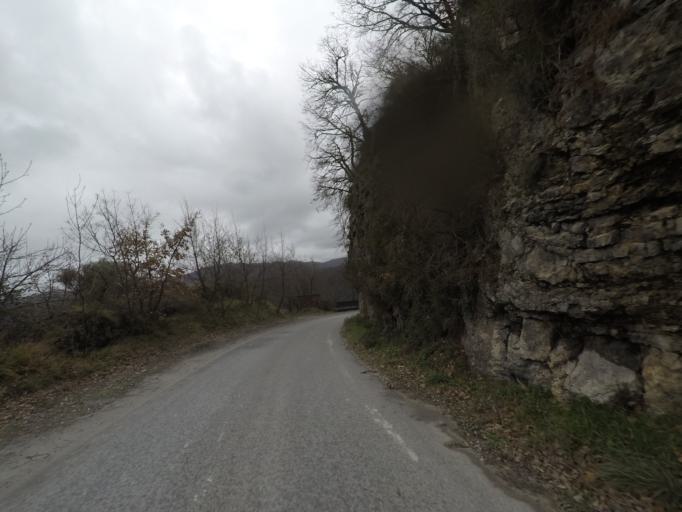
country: IT
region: Tuscany
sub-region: Provincia di Massa-Carrara
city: Carrara
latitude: 44.0845
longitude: 10.1073
